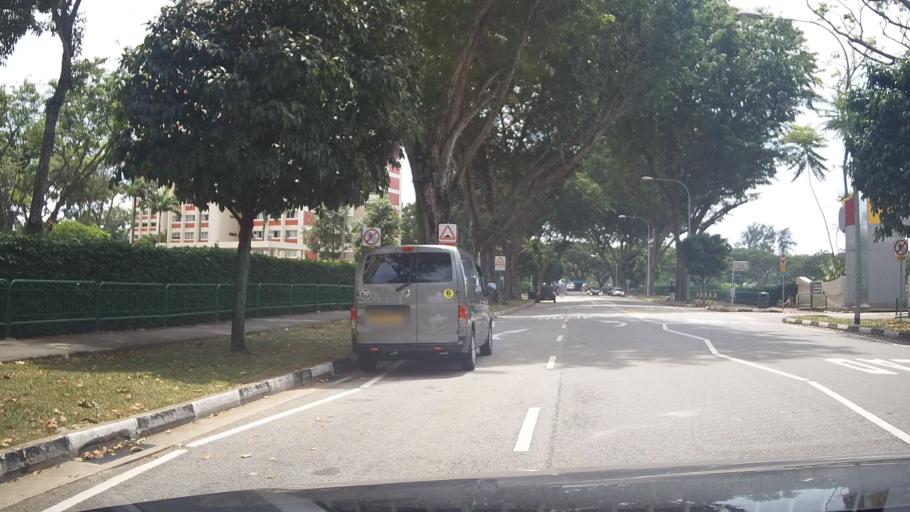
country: SG
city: Singapore
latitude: 1.3070
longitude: 103.9207
